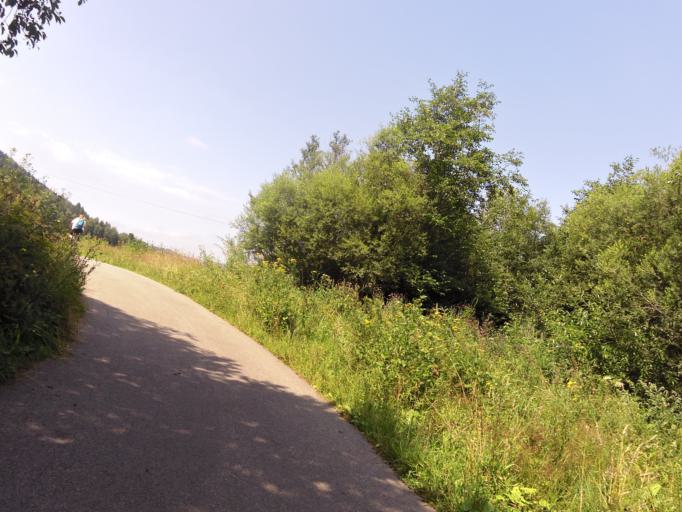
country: PL
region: Silesian Voivodeship
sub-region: Powiat zywiecki
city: Milowka
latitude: 49.5376
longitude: 19.1083
